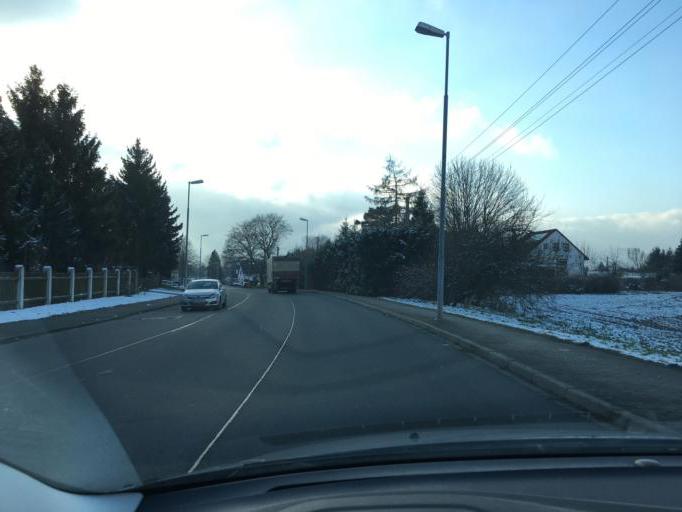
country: DE
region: Saxony
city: Brandis
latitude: 51.3586
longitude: 12.5898
